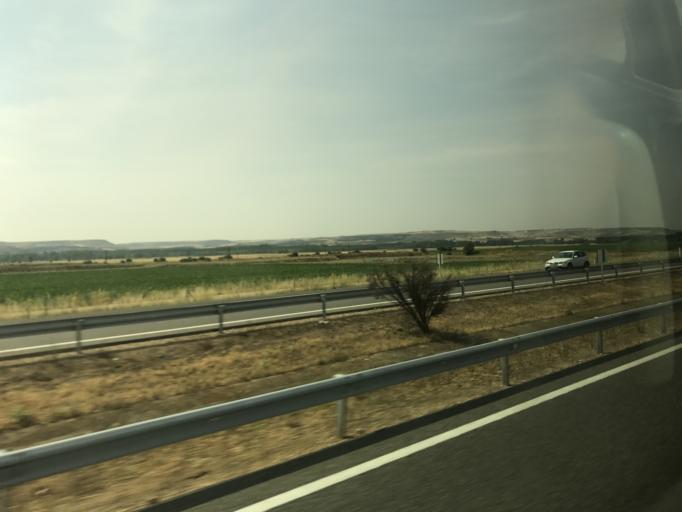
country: ES
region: Castille and Leon
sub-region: Provincia de Burgos
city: Villazopeque
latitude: 42.1938
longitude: -4.0299
